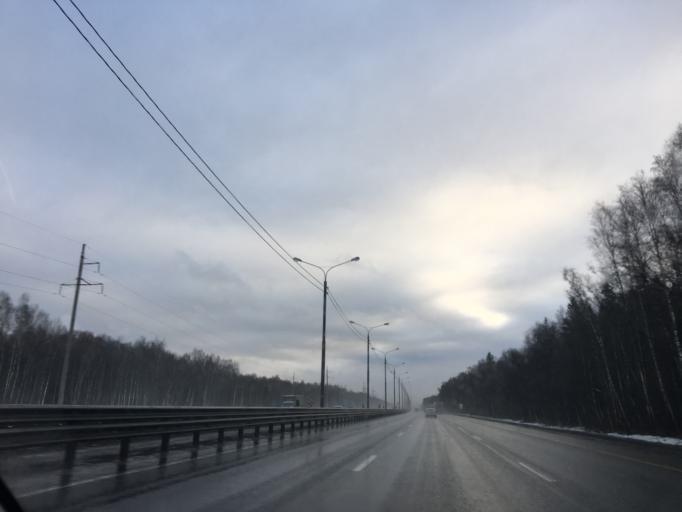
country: RU
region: Moskovskaya
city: L'vovskiy
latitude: 55.2977
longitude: 37.5458
